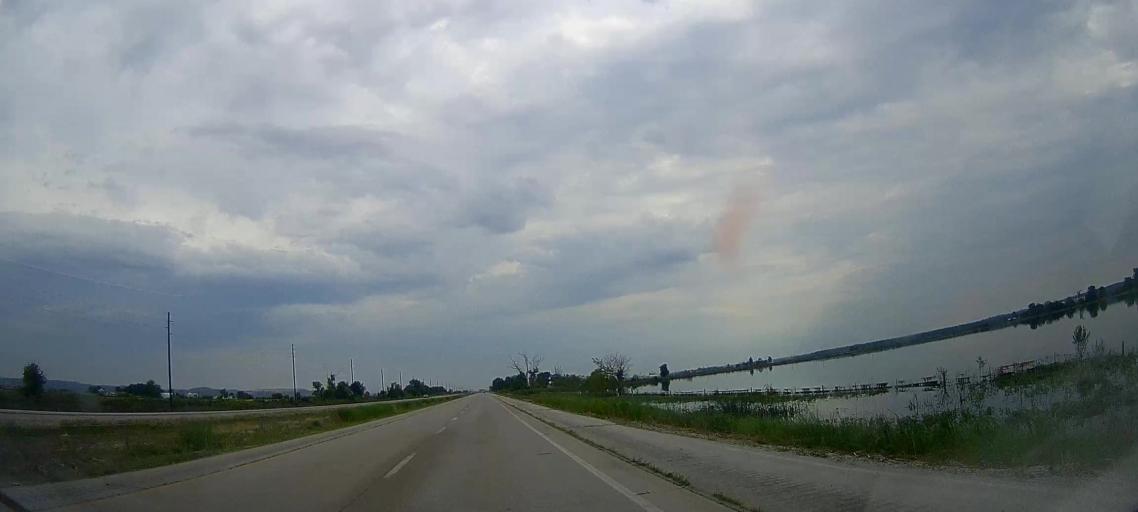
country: US
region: Iowa
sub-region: Pottawattamie County
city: Carter Lake
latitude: 41.4016
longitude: -95.8997
